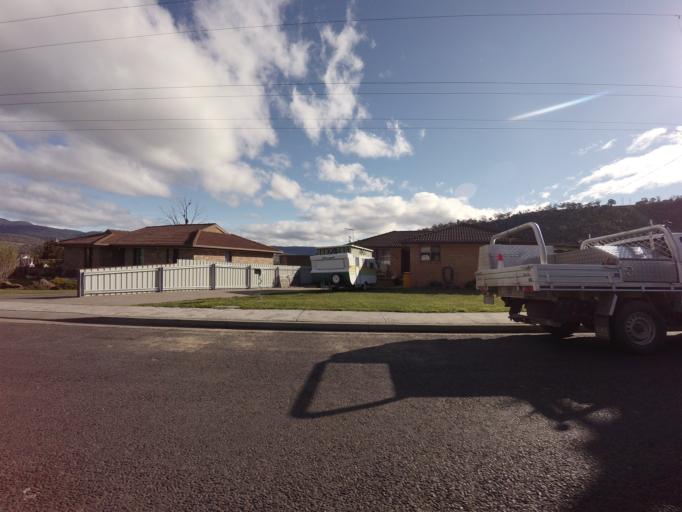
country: AU
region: Tasmania
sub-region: Derwent Valley
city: New Norfolk
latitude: -42.7606
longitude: 147.0472
